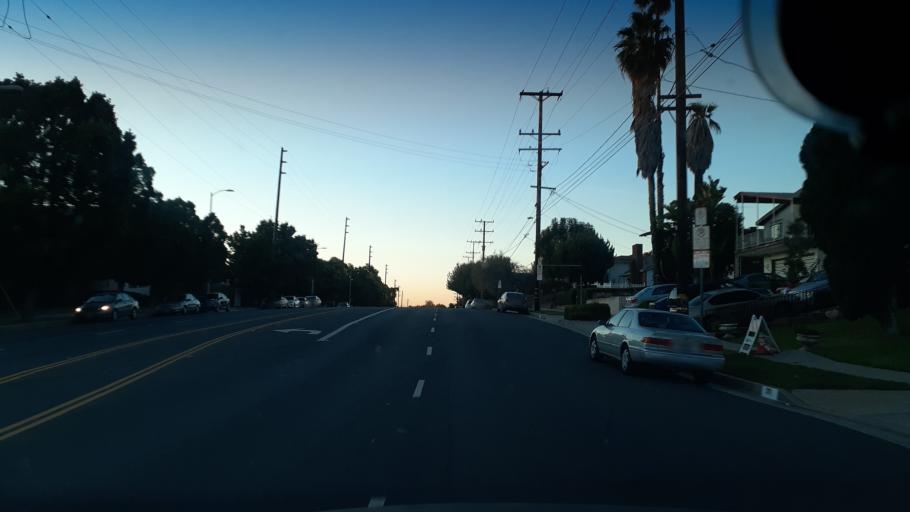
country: US
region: California
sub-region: Los Angeles County
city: San Pedro
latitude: 33.7467
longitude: -118.3097
